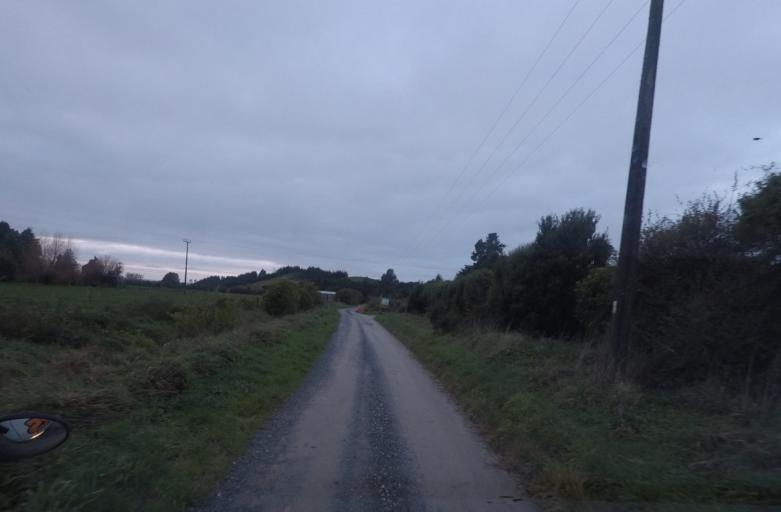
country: NZ
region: Tasman
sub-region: Tasman District
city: Takaka
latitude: -40.7939
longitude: 172.7383
